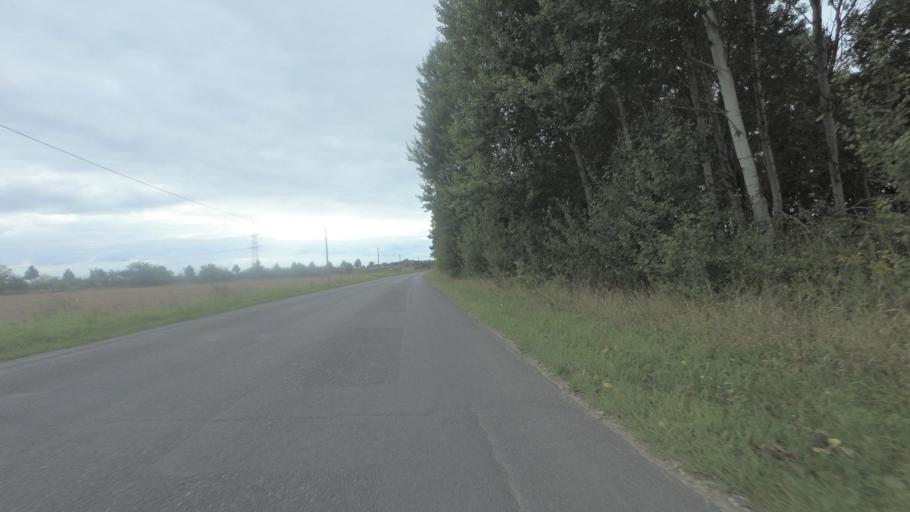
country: DE
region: Brandenburg
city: Hoppegarten
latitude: 52.5556
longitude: 13.6468
